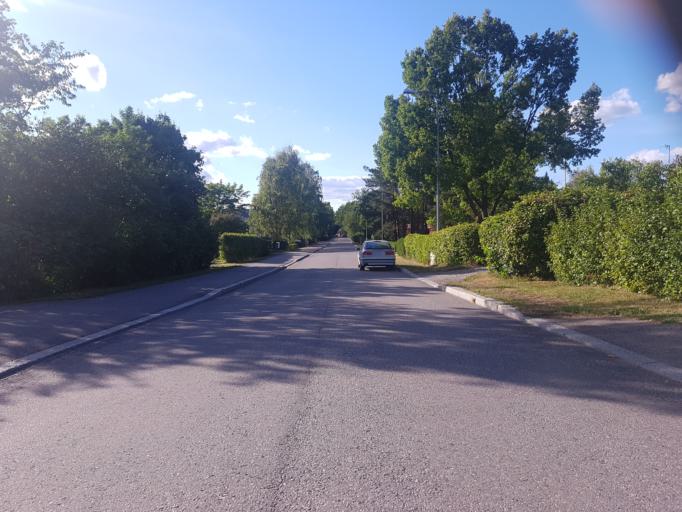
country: FI
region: Uusimaa
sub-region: Helsinki
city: Vantaa
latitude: 60.2831
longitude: 25.0057
